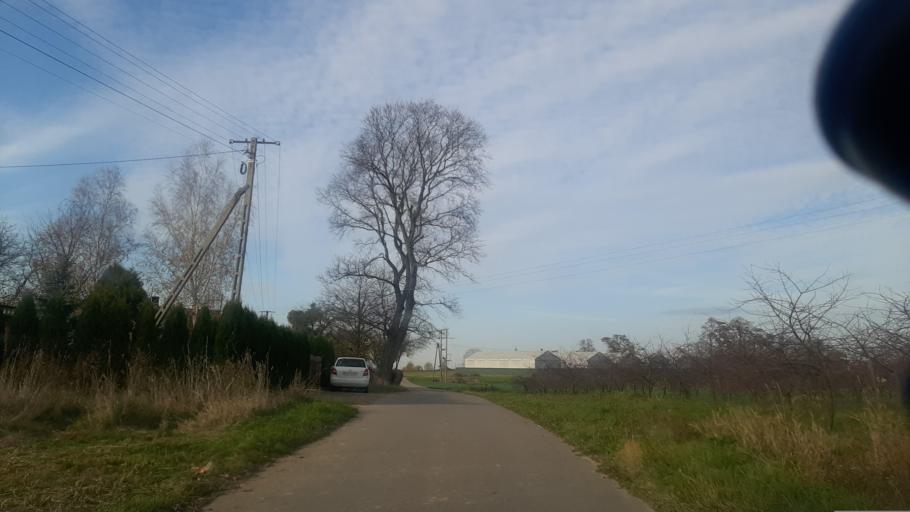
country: PL
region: Lublin Voivodeship
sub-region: Powiat pulawski
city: Markuszow
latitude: 51.3681
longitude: 22.2723
